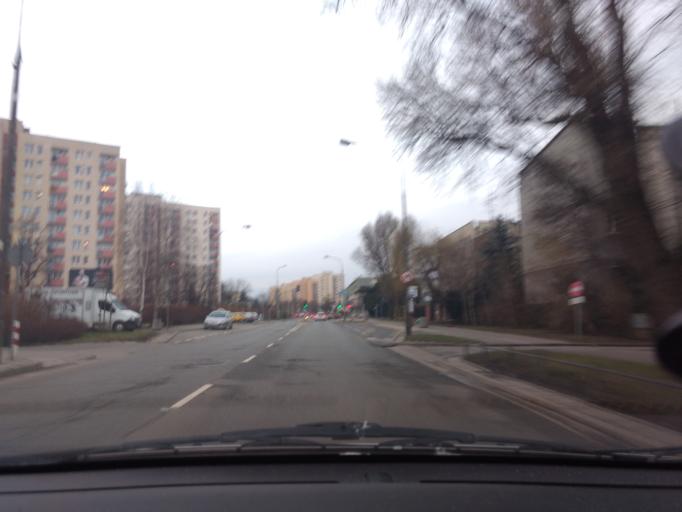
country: PL
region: Masovian Voivodeship
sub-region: Warszawa
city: Praga Poludnie
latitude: 52.2262
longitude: 21.0665
